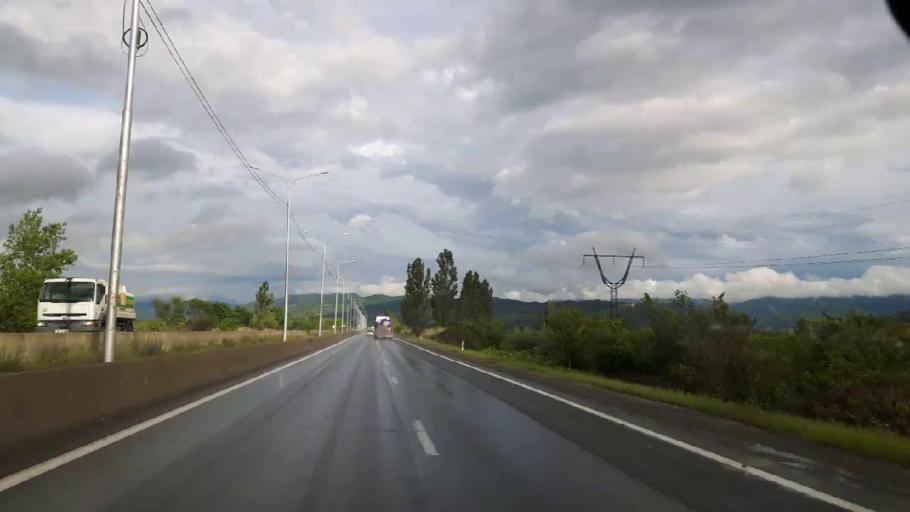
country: GE
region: Shida Kartli
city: Kaspi
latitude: 41.9239
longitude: 44.5411
